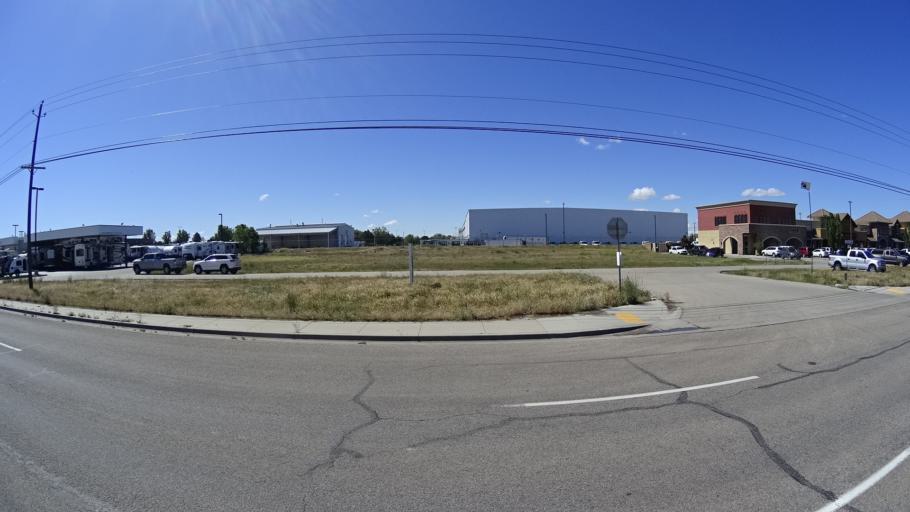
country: US
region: Idaho
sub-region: Ada County
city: Meridian
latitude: 43.6192
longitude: -116.3624
